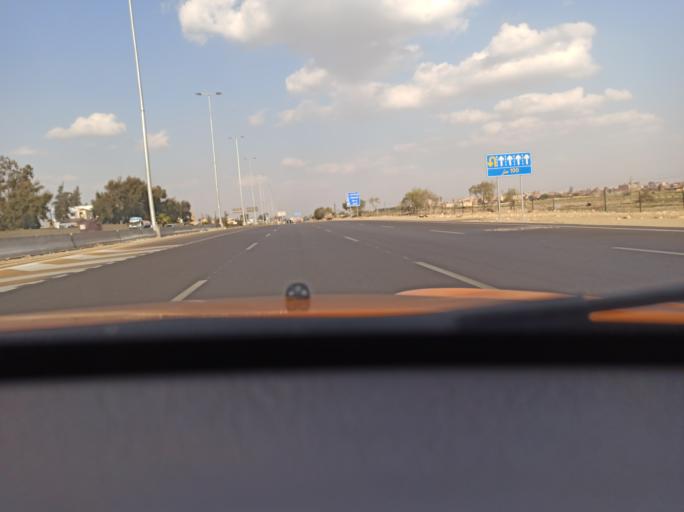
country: EG
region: Al Isma'iliyah
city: Ismailia
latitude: 30.6183
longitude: 32.2331
